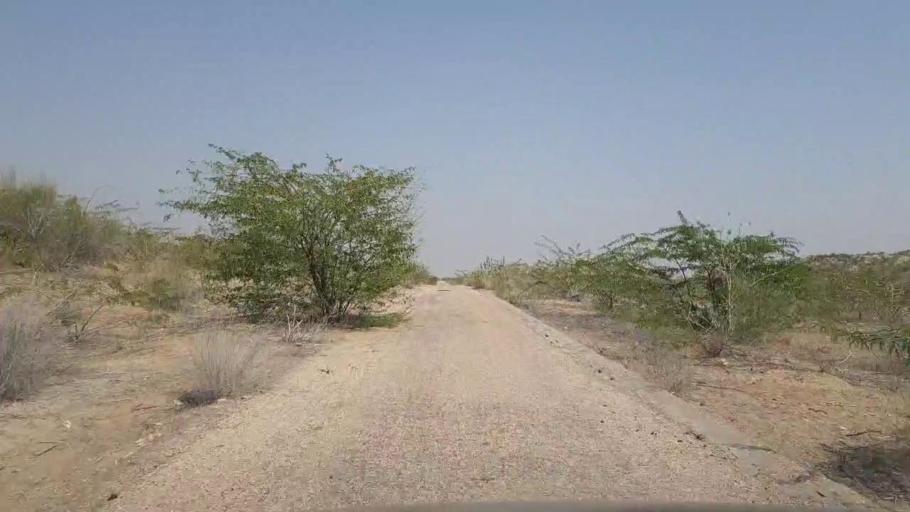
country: PK
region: Sindh
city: Chor
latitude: 25.5877
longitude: 70.2005
